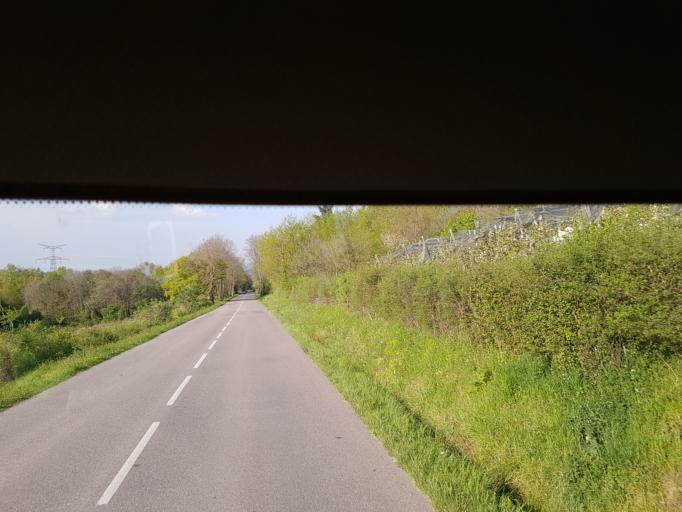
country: FR
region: Rhone-Alpes
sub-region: Departement du Rhone
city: Orlienas
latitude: 45.6485
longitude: 4.6875
